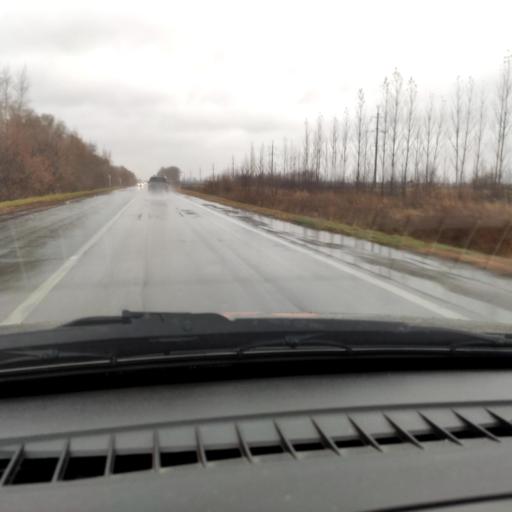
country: RU
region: Samara
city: Tol'yatti
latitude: 53.6188
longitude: 49.3108
